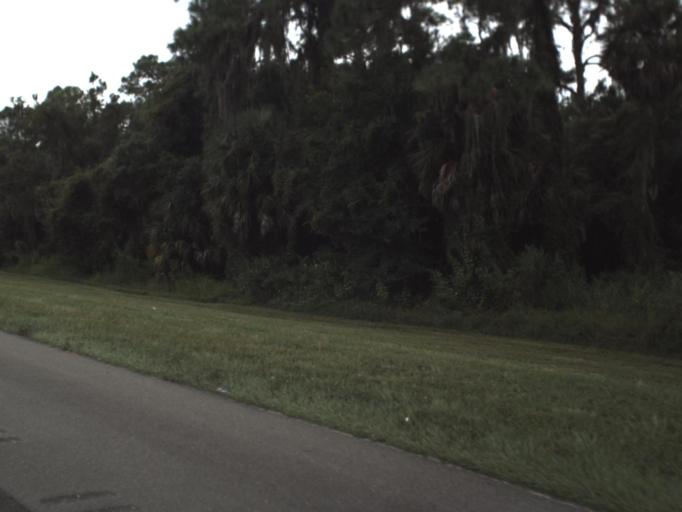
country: US
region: Florida
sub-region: Sarasota County
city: The Meadows
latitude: 27.4049
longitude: -82.4535
